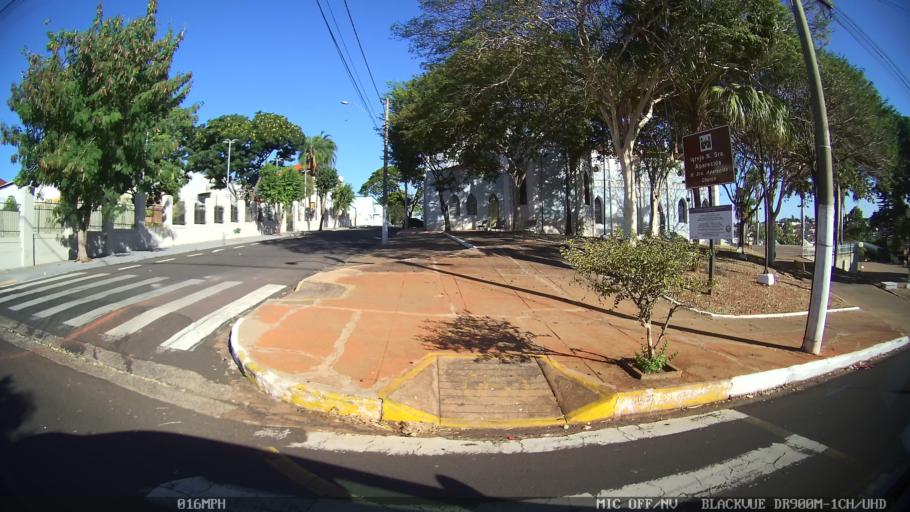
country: BR
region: Sao Paulo
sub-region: Olimpia
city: Olimpia
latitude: -20.7366
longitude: -48.9090
